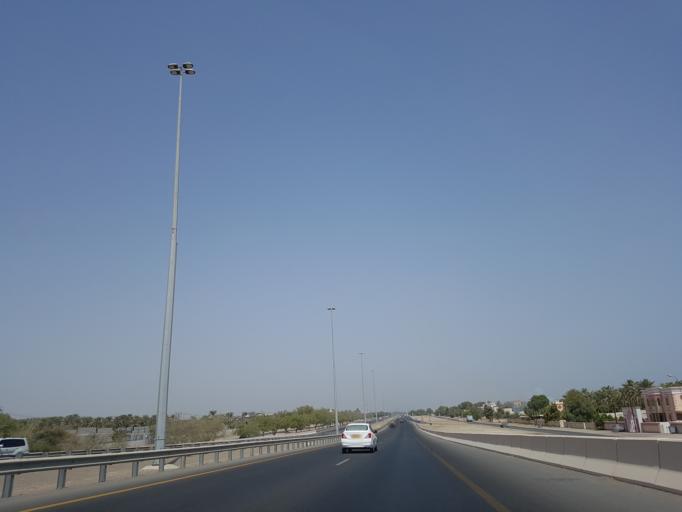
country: OM
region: Al Batinah
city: Saham
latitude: 24.0763
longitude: 56.9442
